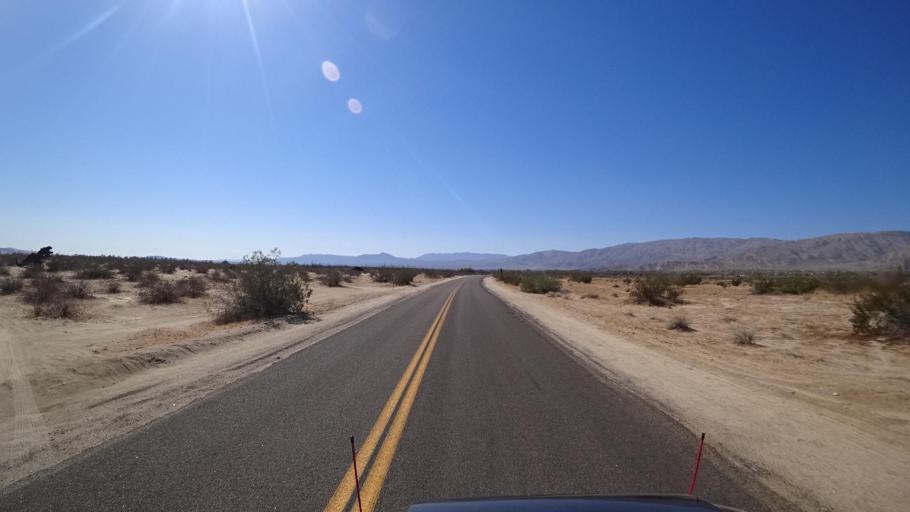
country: US
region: California
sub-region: San Diego County
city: Borrego Springs
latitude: 33.2882
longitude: -116.3757
